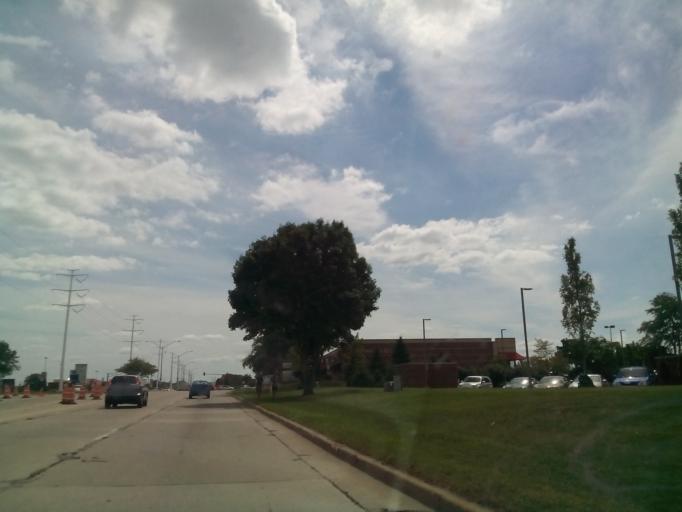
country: US
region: Illinois
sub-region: DuPage County
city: Naperville
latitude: 41.7612
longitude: -88.2061
